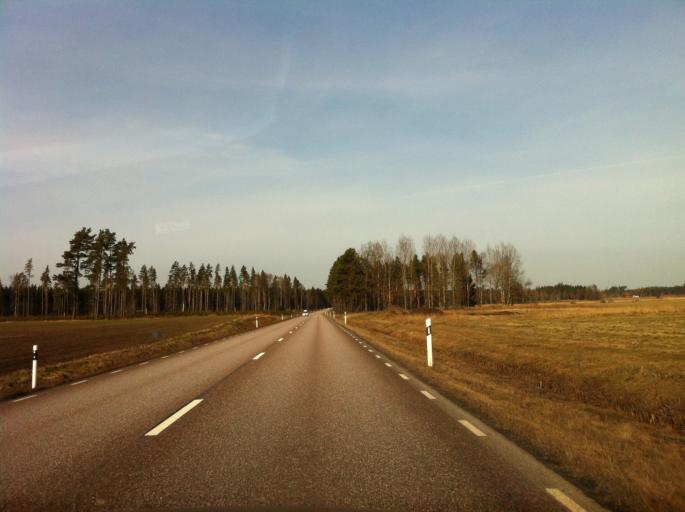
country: SE
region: Vaestra Goetaland
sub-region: Skovde Kommun
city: Skultorp
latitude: 58.2579
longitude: 13.8121
